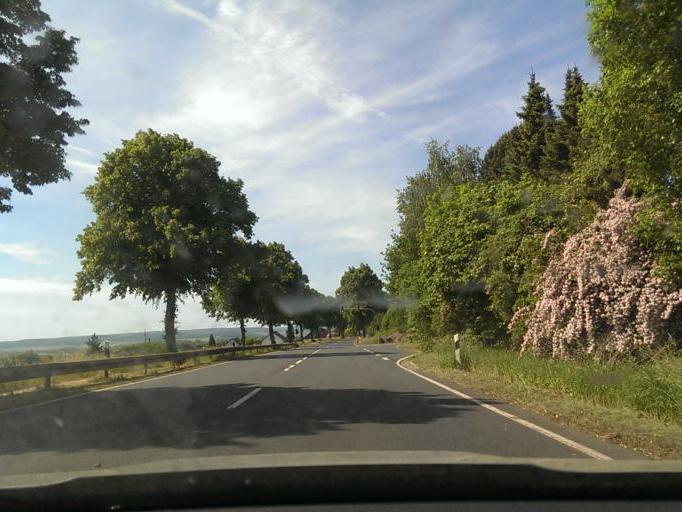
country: DE
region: Lower Saxony
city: Elze
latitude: 52.1302
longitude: 9.7480
